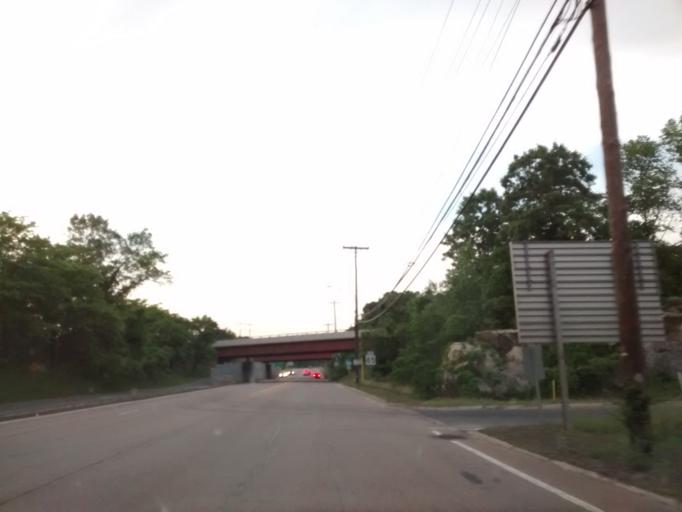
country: US
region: Massachusetts
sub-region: Worcester County
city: Milford
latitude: 42.1651
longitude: -71.5086
